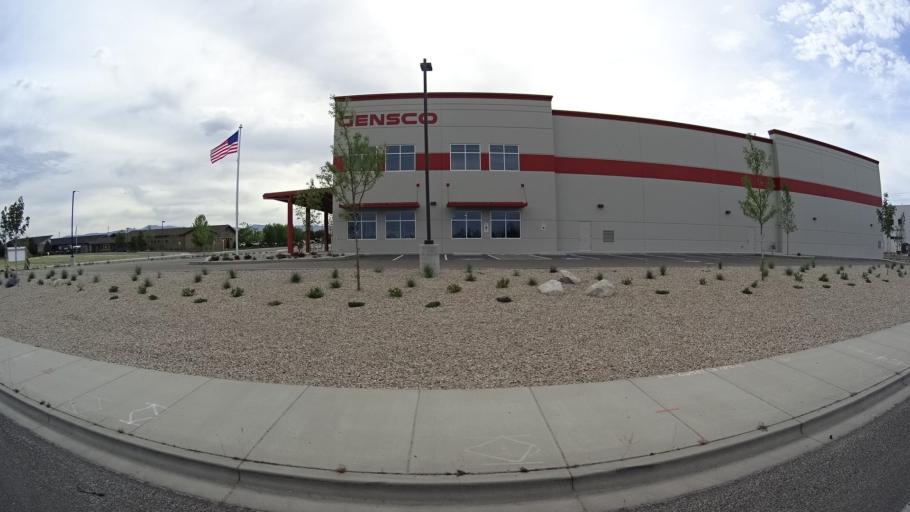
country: US
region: Idaho
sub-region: Ada County
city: Meridian
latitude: 43.6064
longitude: -116.3745
